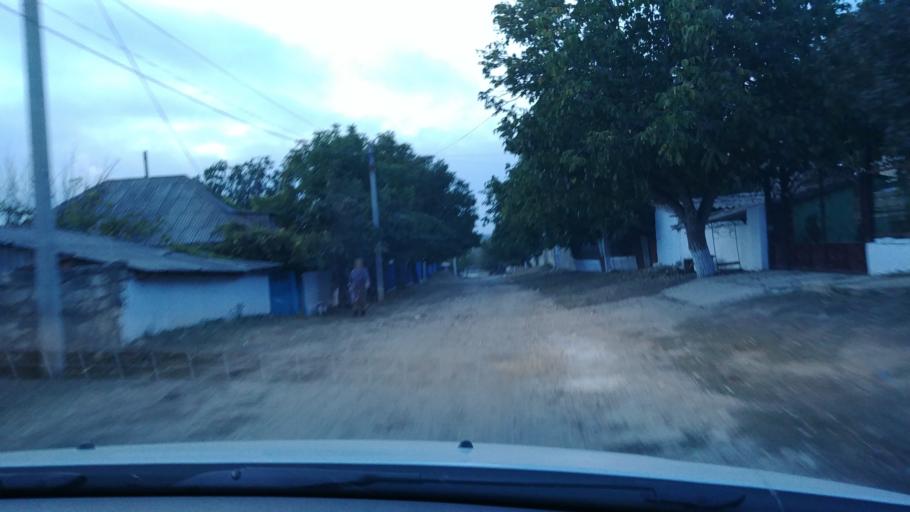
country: MD
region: Rezina
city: Saharna
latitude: 47.6780
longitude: 28.9594
